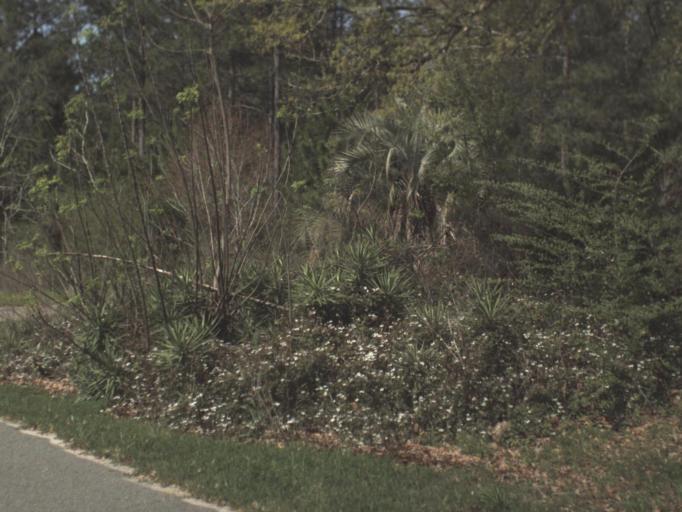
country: US
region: Florida
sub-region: Jackson County
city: Graceville
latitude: 30.9472
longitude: -85.4046
